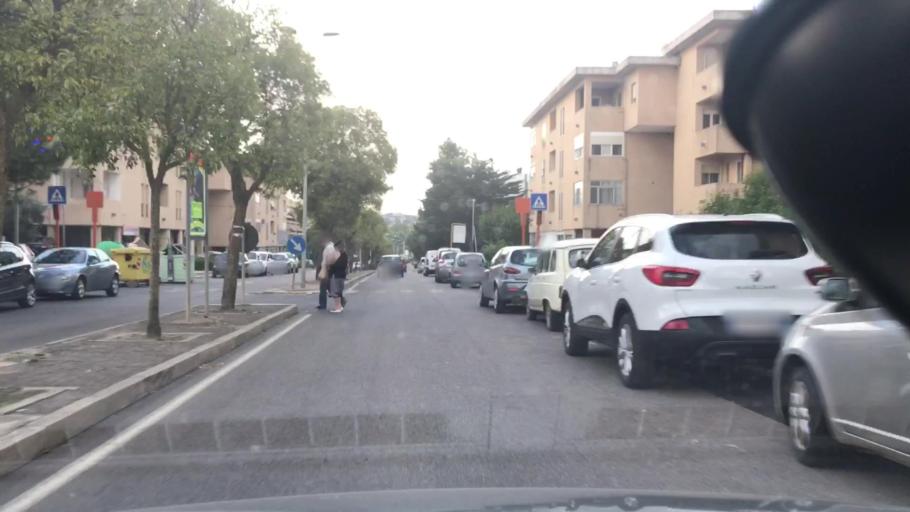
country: IT
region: Basilicate
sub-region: Provincia di Matera
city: Matera
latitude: 40.6831
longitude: 16.5854
